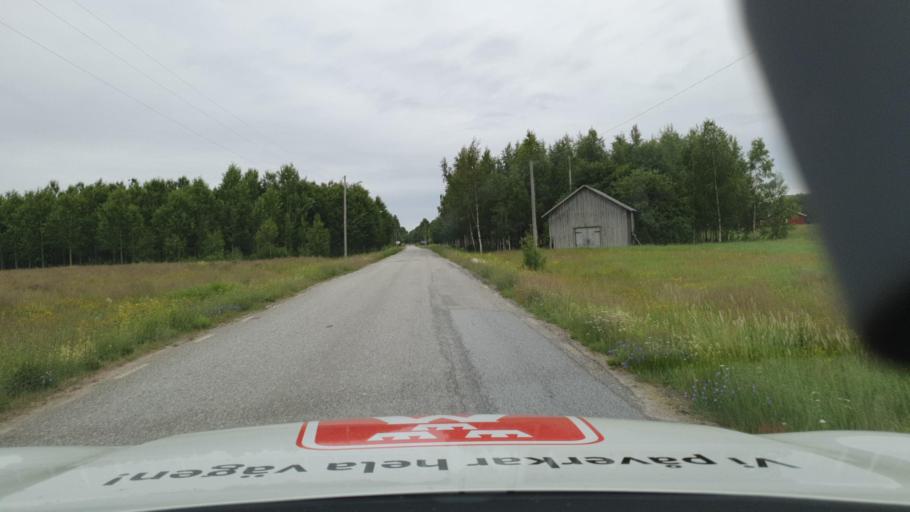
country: SE
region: Vaesterbotten
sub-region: Nordmalings Kommun
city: Nordmaling
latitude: 63.5402
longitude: 19.3956
